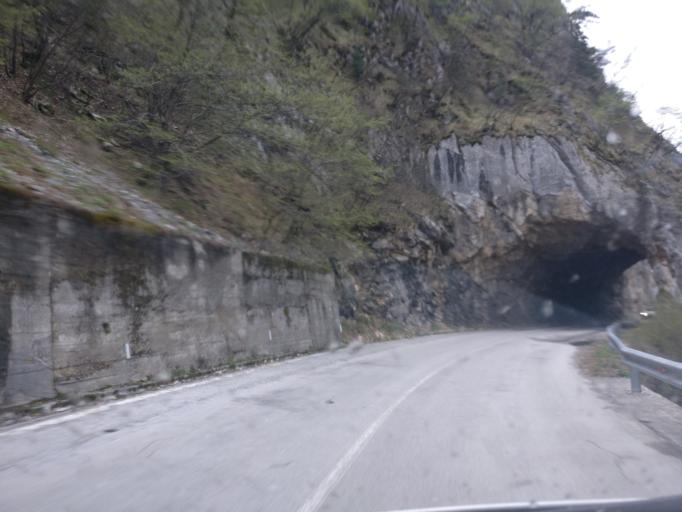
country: ME
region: Opstina Pluzine
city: Pluzine
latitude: 43.2390
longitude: 18.8423
